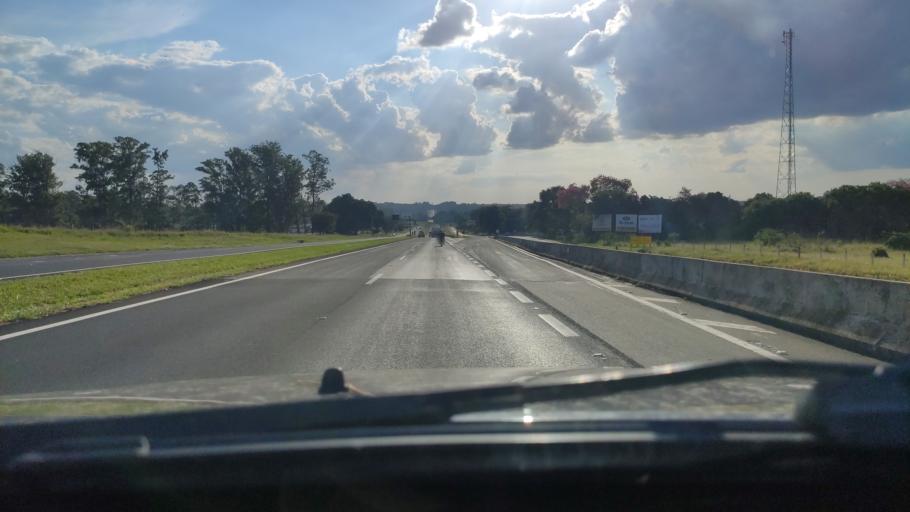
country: BR
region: Sao Paulo
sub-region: Mogi-Mirim
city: Mogi Mirim
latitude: -22.4555
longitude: -46.9180
